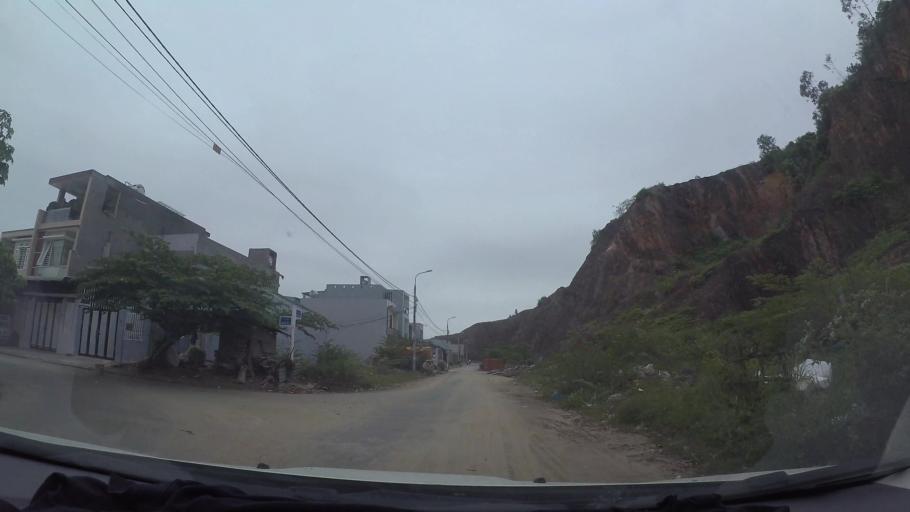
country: VN
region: Da Nang
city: Lien Chieu
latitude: 16.0652
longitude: 108.1452
